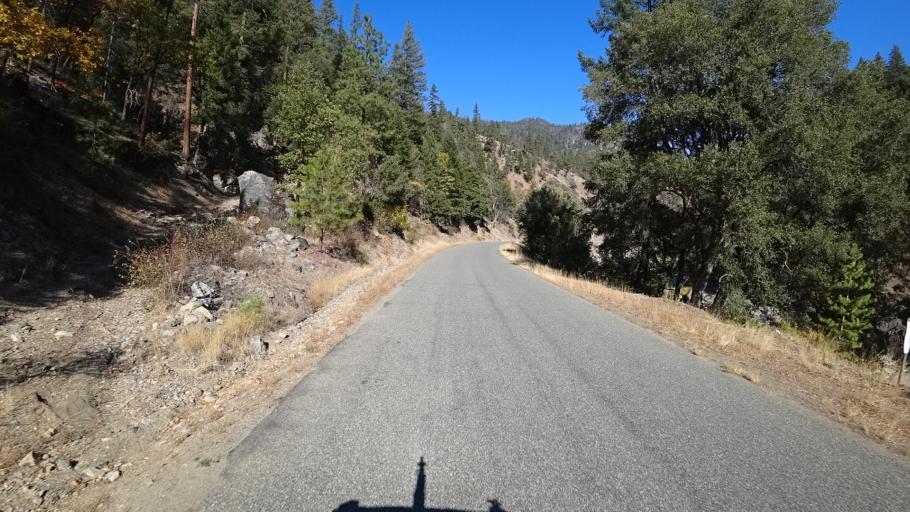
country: US
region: California
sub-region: Siskiyou County
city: Happy Camp
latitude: 41.6624
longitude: -123.1144
